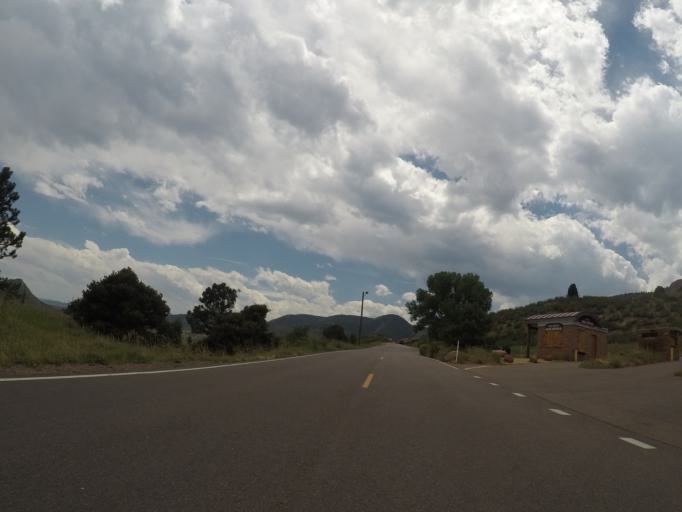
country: US
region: Colorado
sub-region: Jefferson County
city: Indian Hills
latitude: 39.6686
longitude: -105.1976
